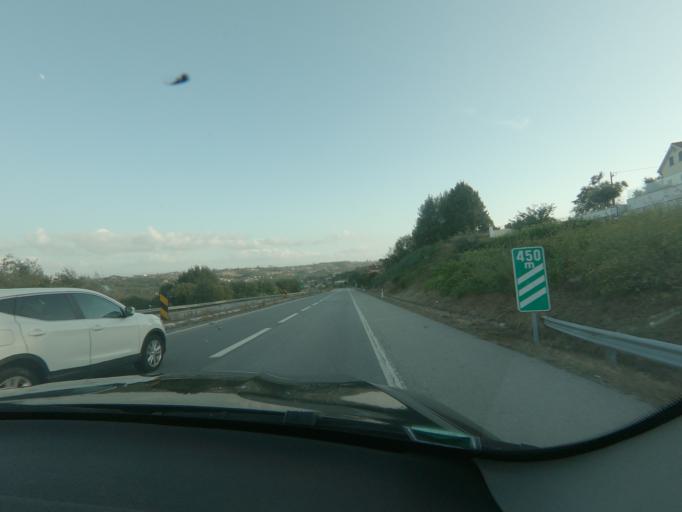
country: PT
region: Viseu
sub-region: Santa Comba Dao
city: Santa Comba Dao
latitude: 40.4053
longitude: -8.1256
